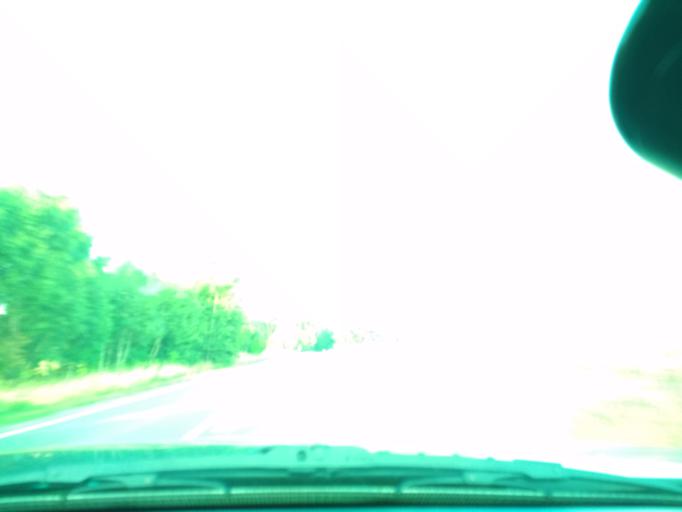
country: PL
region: Lesser Poland Voivodeship
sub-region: Powiat olkuski
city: Zarzecze
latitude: 50.3979
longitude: 19.7200
